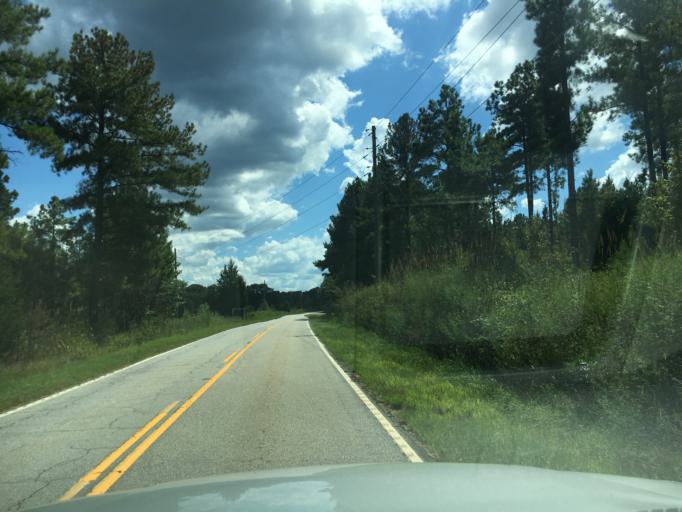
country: US
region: South Carolina
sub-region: Laurens County
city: Laurens
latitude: 34.5203
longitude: -82.0933
